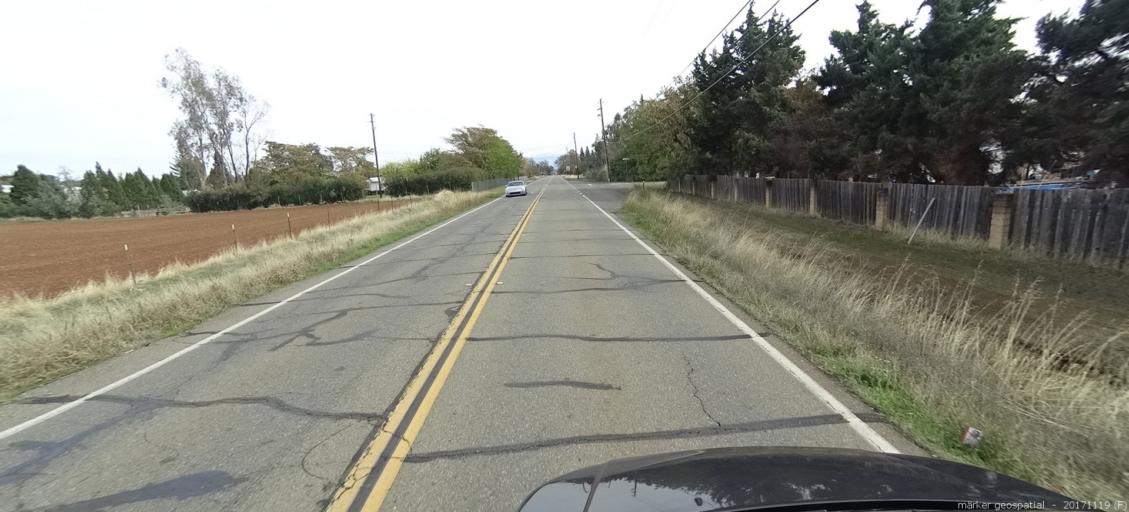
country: US
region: California
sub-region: Shasta County
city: Anderson
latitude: 40.4804
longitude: -122.2715
